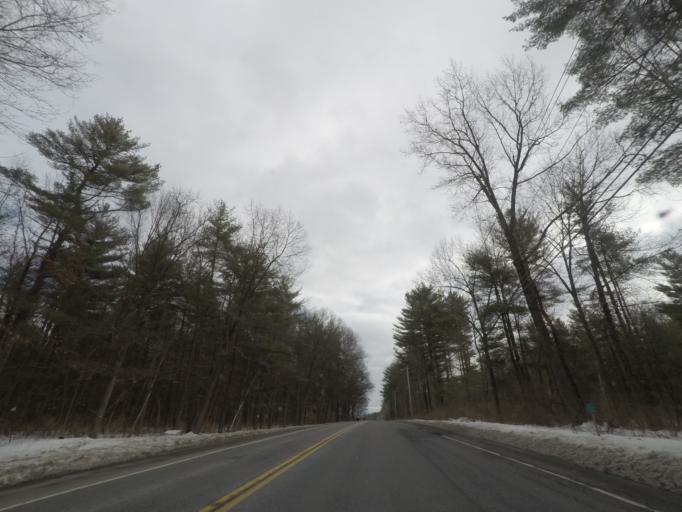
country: US
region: New York
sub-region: Saratoga County
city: Schuylerville
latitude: 43.0943
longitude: -73.5604
